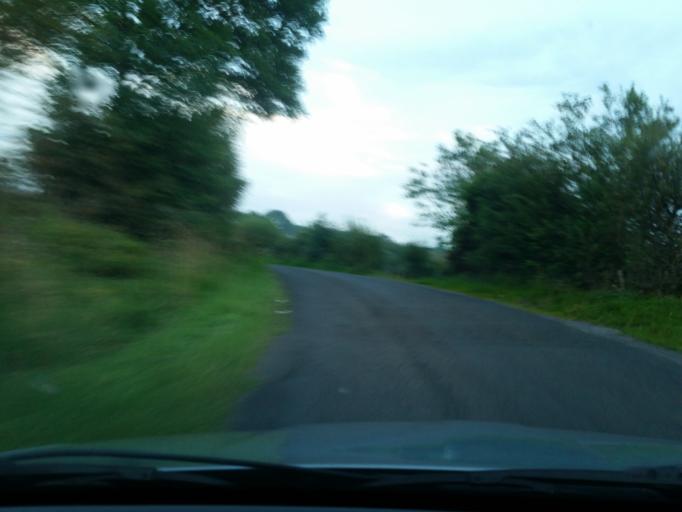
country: GB
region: Northern Ireland
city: Fivemiletown
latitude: 54.2885
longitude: -7.2795
